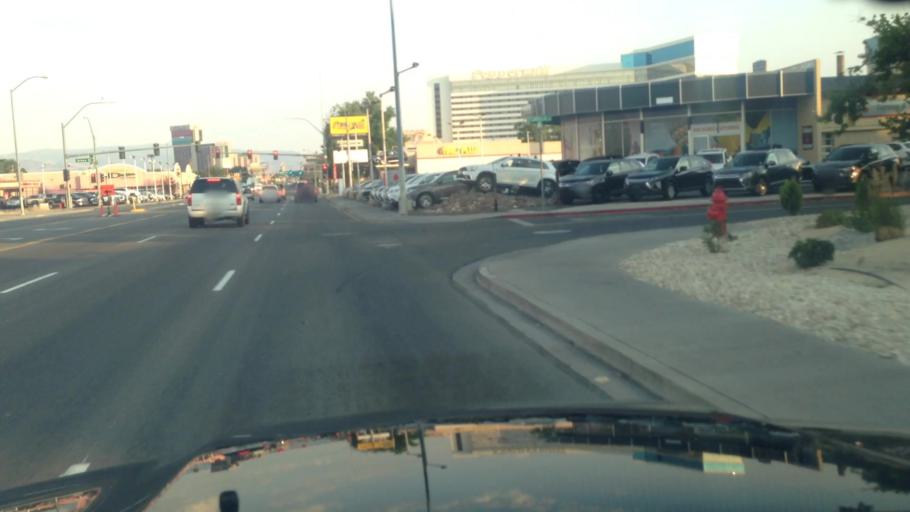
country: US
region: Nevada
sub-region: Washoe County
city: Reno
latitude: 39.5017
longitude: -119.8014
